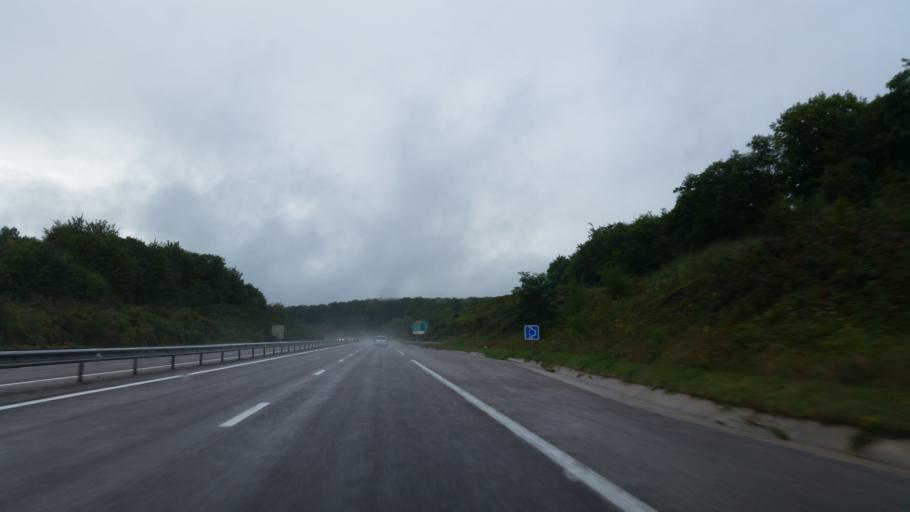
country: FR
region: Franche-Comte
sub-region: Departement de la Haute-Saone
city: Hericourt
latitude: 47.6026
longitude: 6.7185
